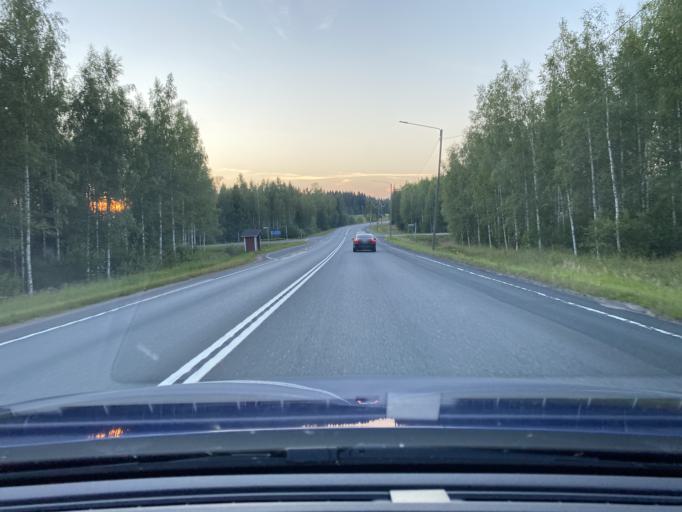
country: FI
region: Pirkanmaa
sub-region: Luoteis-Pirkanmaa
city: Ikaalinen
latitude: 61.8446
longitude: 22.9319
